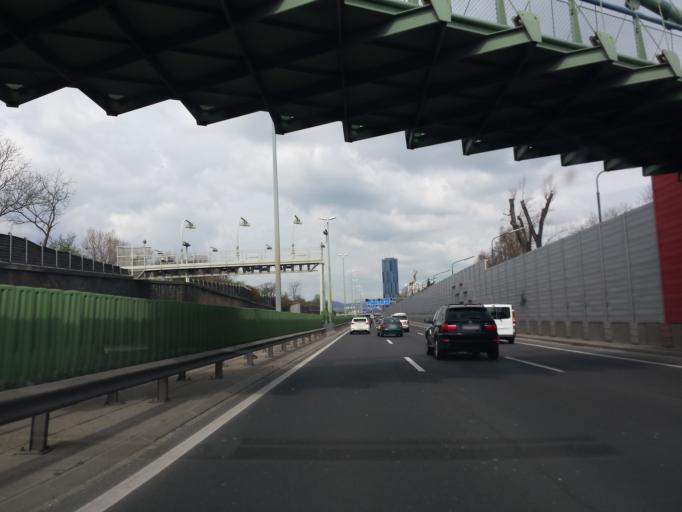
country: AT
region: Vienna
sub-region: Wien Stadt
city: Vienna
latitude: 48.2156
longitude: 16.4342
